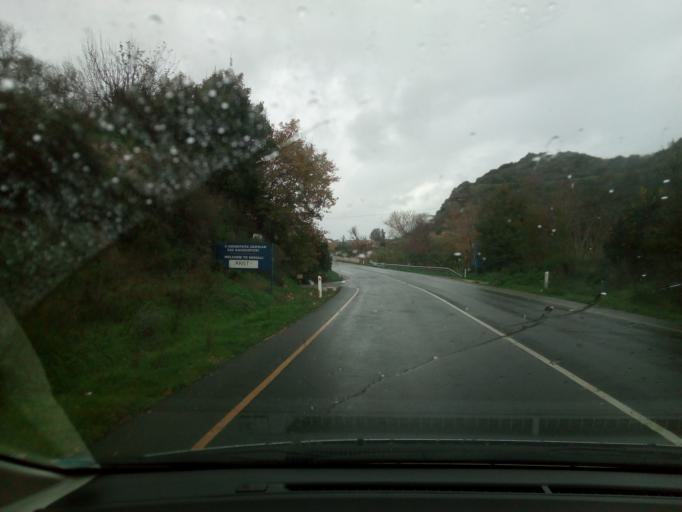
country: CY
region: Pafos
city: Polis
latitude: 34.9761
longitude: 32.4504
